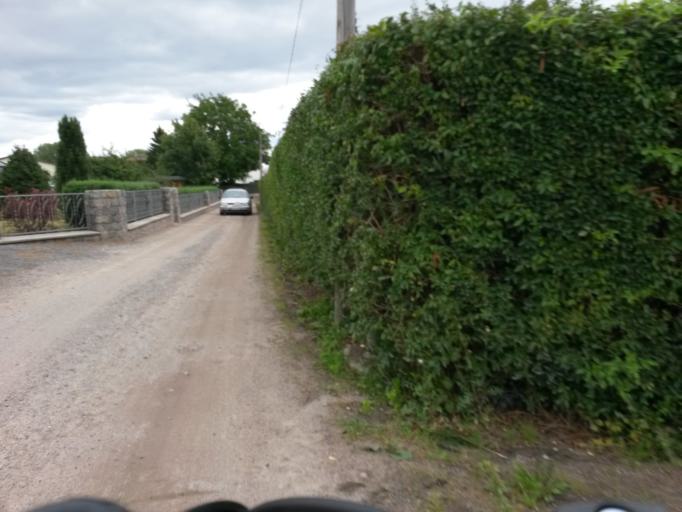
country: DE
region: Brandenburg
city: Angermunde
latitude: 53.0144
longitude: 14.0049
